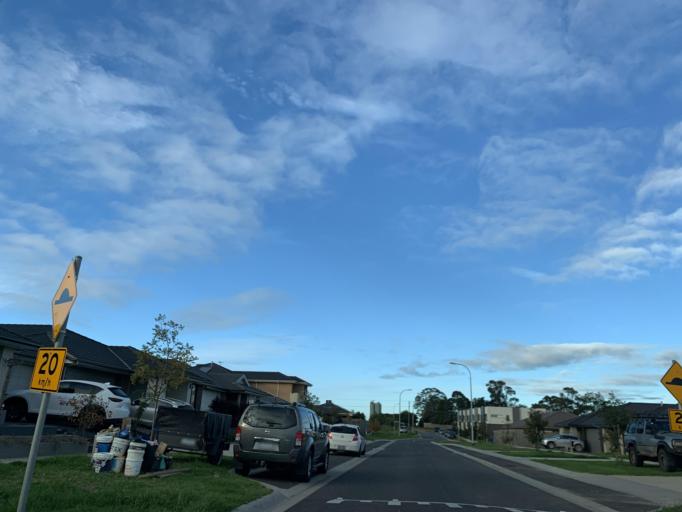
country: AU
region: Victoria
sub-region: Casey
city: Junction Village
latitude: -38.1310
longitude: 145.3210
